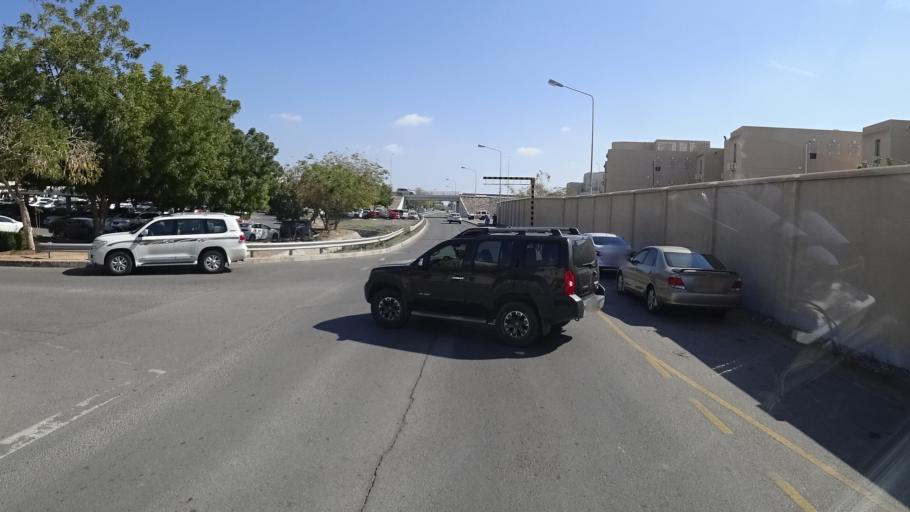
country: OM
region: Muhafazat Masqat
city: As Sib al Jadidah
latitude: 23.5861
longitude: 58.1695
